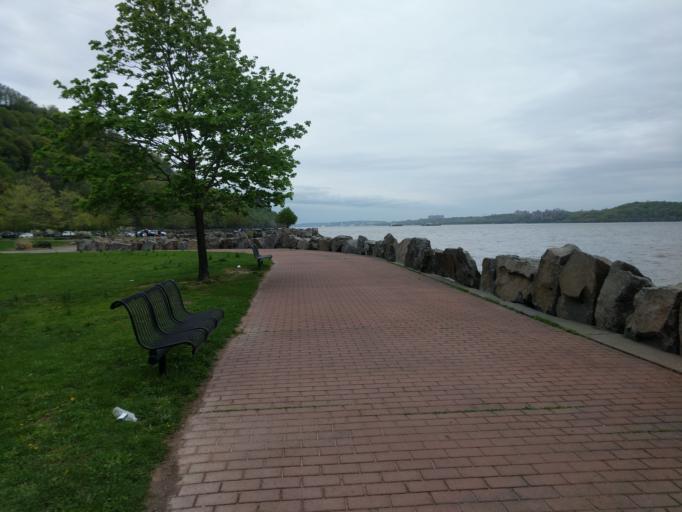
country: US
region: New Jersey
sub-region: Bergen County
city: Fort Lee
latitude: 40.8598
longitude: -73.9545
